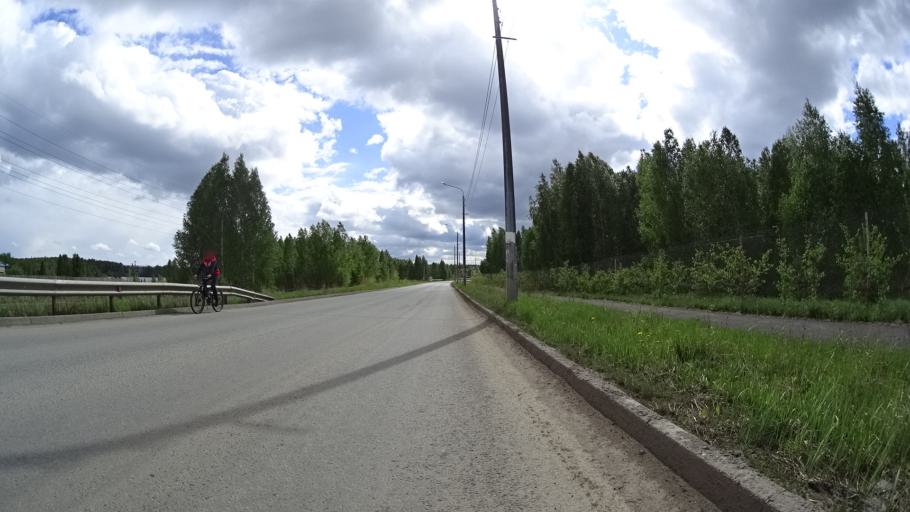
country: RU
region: Chelyabinsk
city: Sargazy
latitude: 55.1537
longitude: 61.2656
